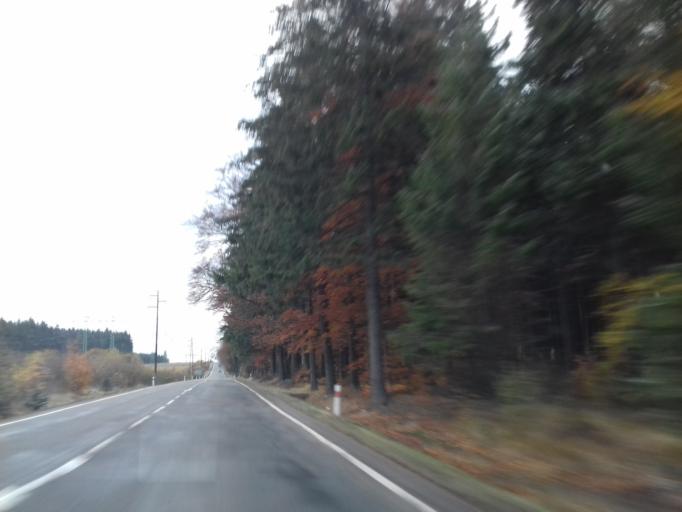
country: CZ
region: Pardubicky
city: Prosec
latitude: 49.7559
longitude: 16.1279
